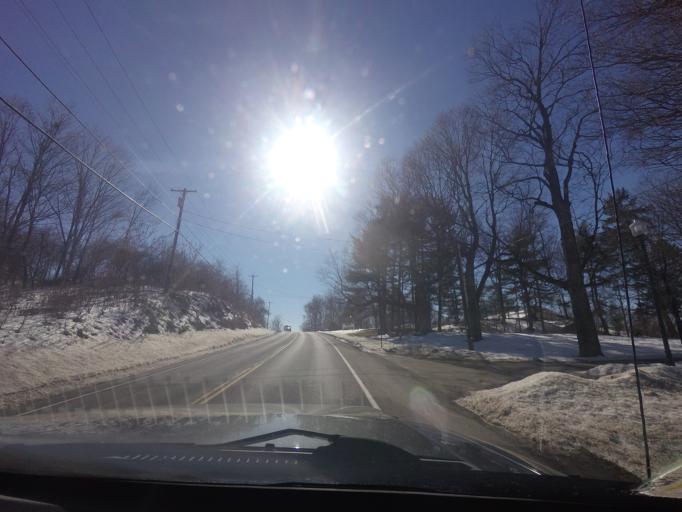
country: US
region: New York
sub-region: Saratoga County
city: Waterford
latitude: 42.8177
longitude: -73.6329
